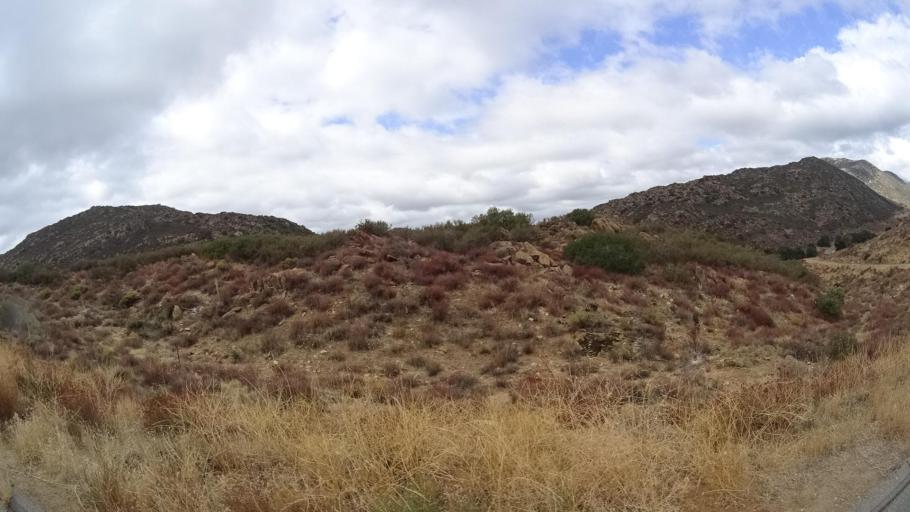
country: US
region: California
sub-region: San Diego County
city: Pine Valley
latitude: 32.7483
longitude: -116.4509
